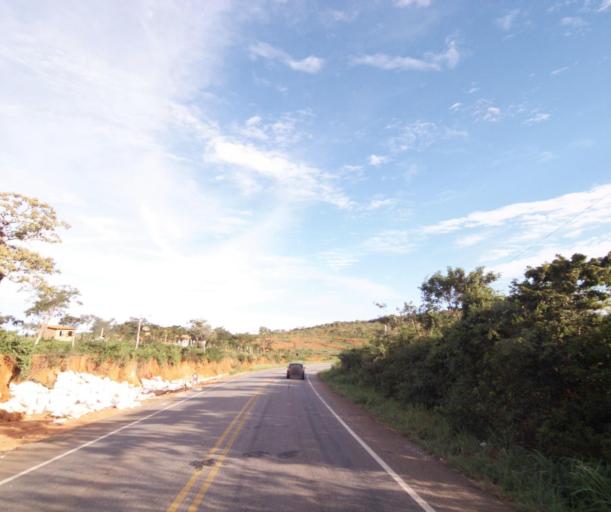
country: BR
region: Bahia
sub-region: Caetite
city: Caetite
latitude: -14.0892
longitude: -42.4480
